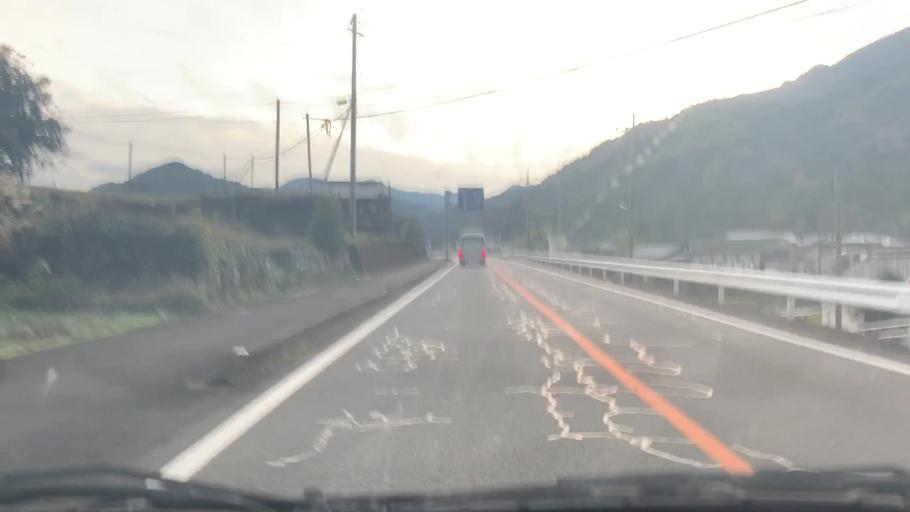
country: JP
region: Saga Prefecture
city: Kashima
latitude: 33.0793
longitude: 130.0680
